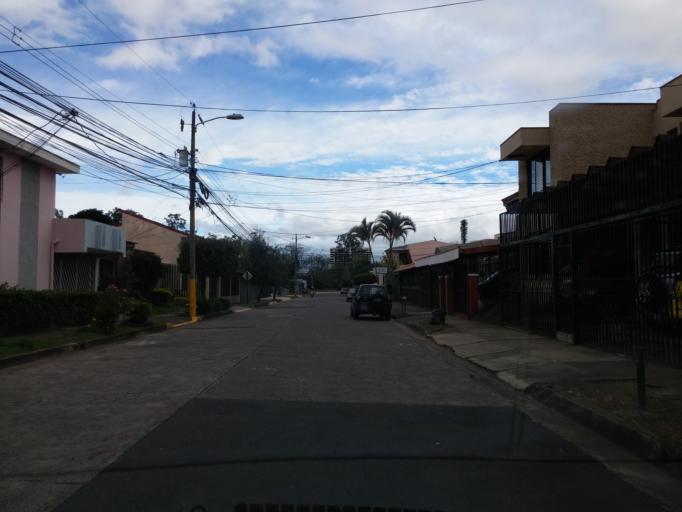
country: CR
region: San Jose
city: San Jose
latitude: 9.9314
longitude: -84.1060
